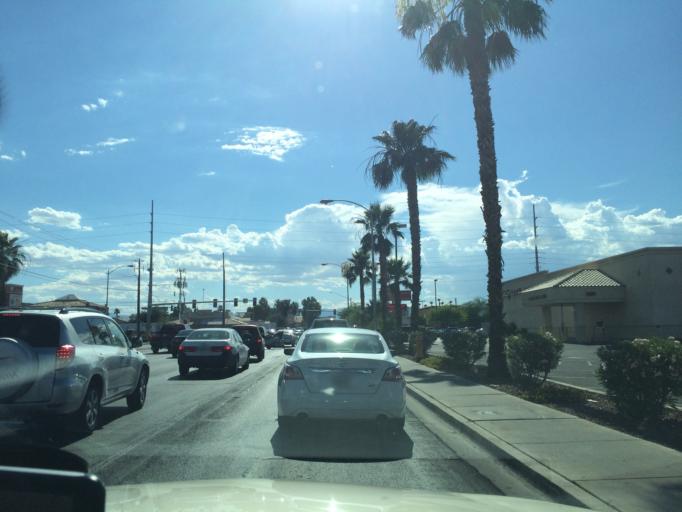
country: US
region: Nevada
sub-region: Clark County
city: Paradise
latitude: 36.1001
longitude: -115.1177
